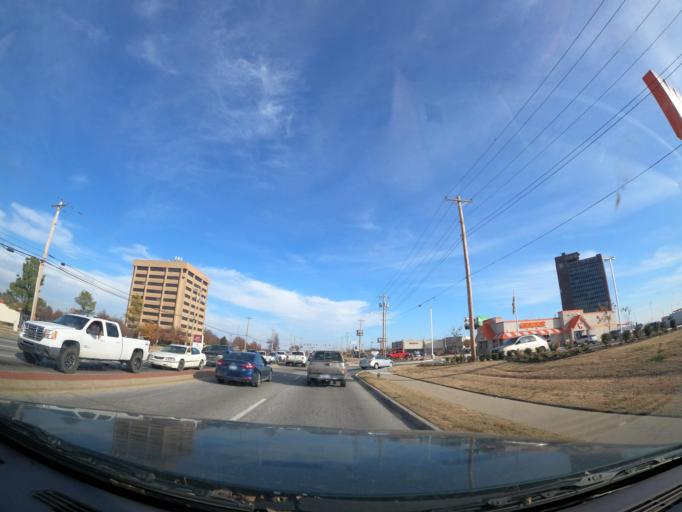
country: US
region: Oklahoma
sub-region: Tulsa County
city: Tulsa
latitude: 36.1043
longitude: -95.9129
